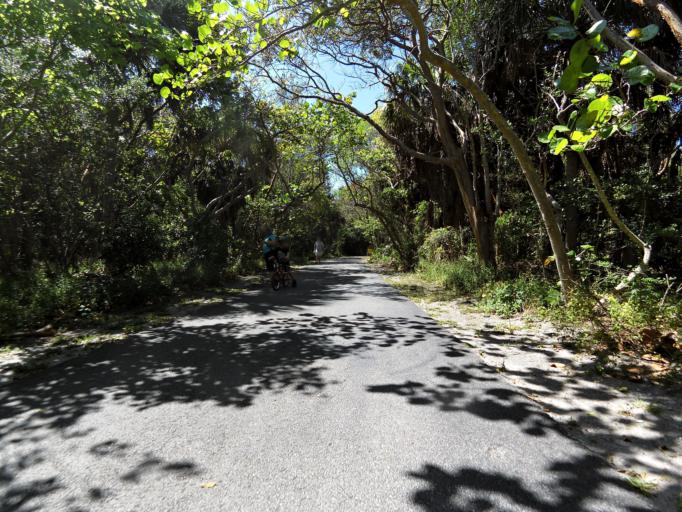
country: US
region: Florida
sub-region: Miami-Dade County
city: Key Biscayne
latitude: 25.6745
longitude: -80.1614
